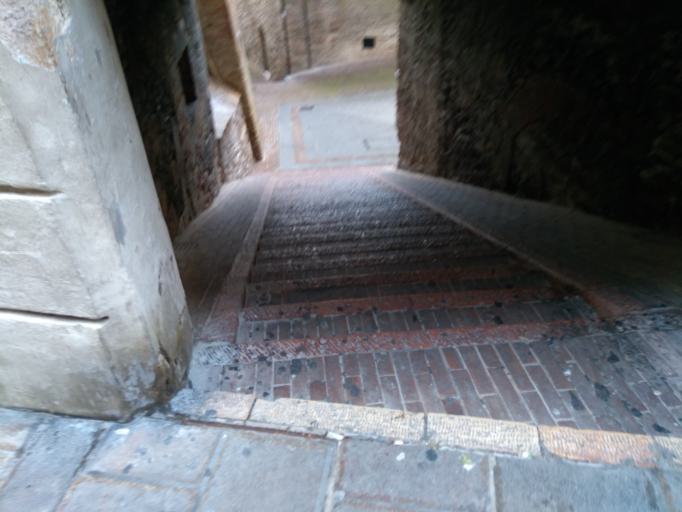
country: IT
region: Umbria
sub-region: Provincia di Perugia
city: Assisi
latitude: 43.0705
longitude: 12.6159
